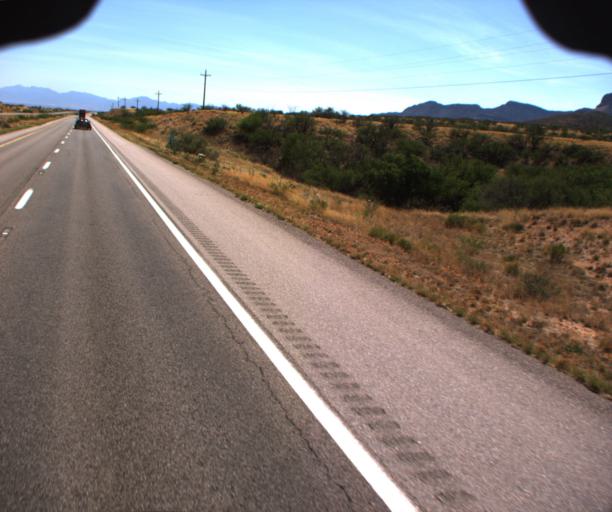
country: US
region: Arizona
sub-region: Cochise County
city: Whetstone
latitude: 31.8572
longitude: -110.3413
